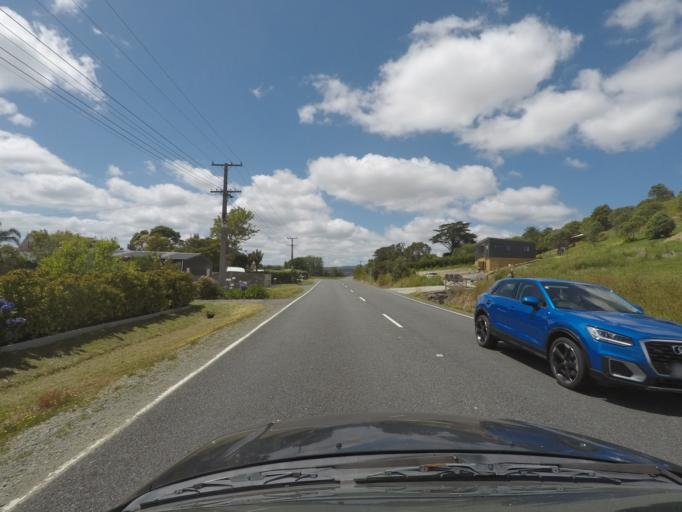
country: NZ
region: Northland
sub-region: Whangarei
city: Ruakaka
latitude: -35.9954
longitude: 174.4720
